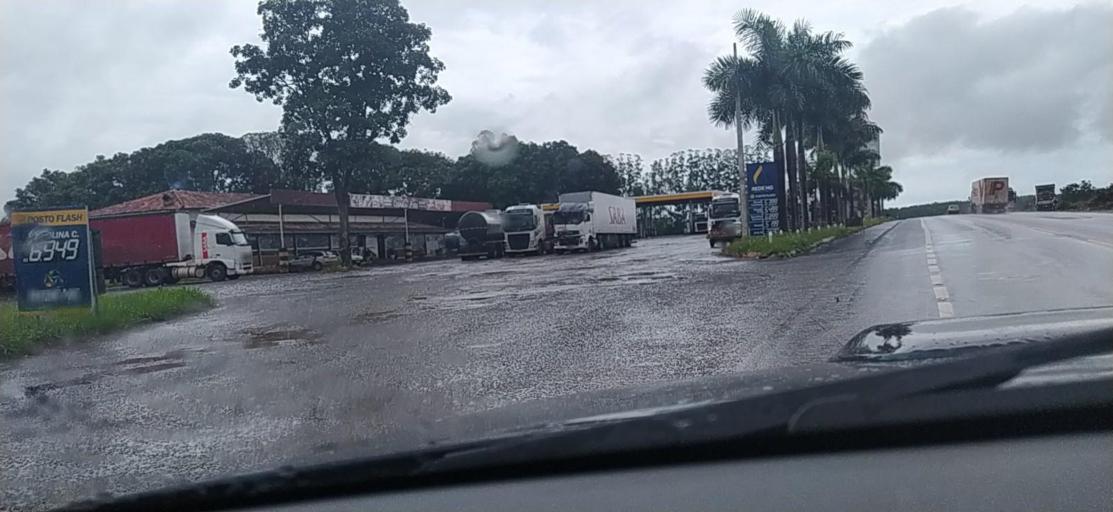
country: BR
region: Minas Gerais
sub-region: Curvelo
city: Curvelo
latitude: -18.9404
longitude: -44.4972
